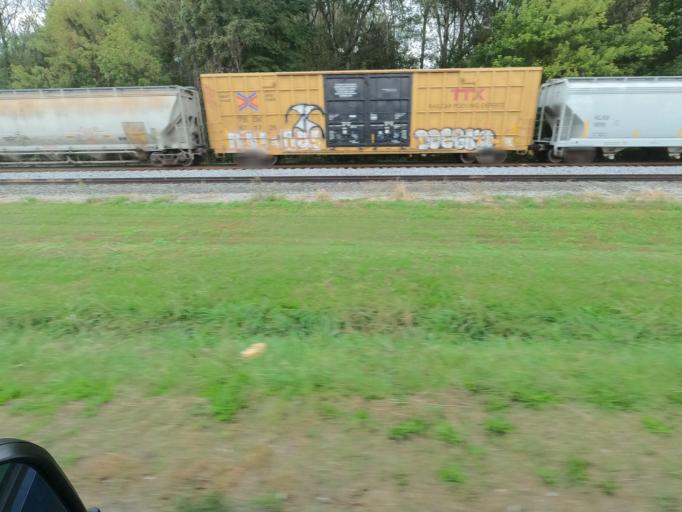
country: US
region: Tennessee
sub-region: Cheatham County
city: Pegram
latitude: 36.1033
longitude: -87.0560
